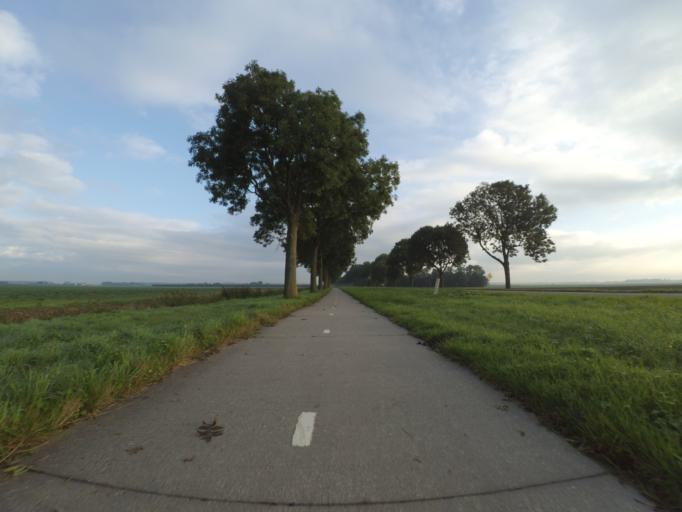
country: NL
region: Flevoland
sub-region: Gemeente Dronten
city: Biddinghuizen
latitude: 52.4929
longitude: 5.6739
